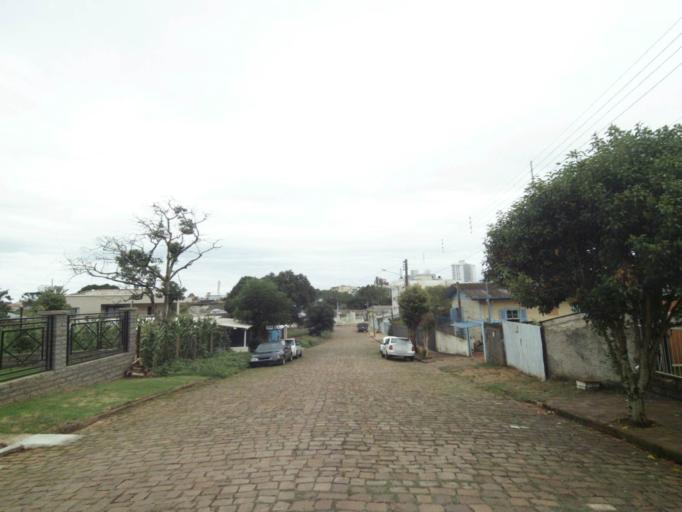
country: BR
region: Rio Grande do Sul
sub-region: Lagoa Vermelha
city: Lagoa Vermelha
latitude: -28.2159
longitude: -51.5205
